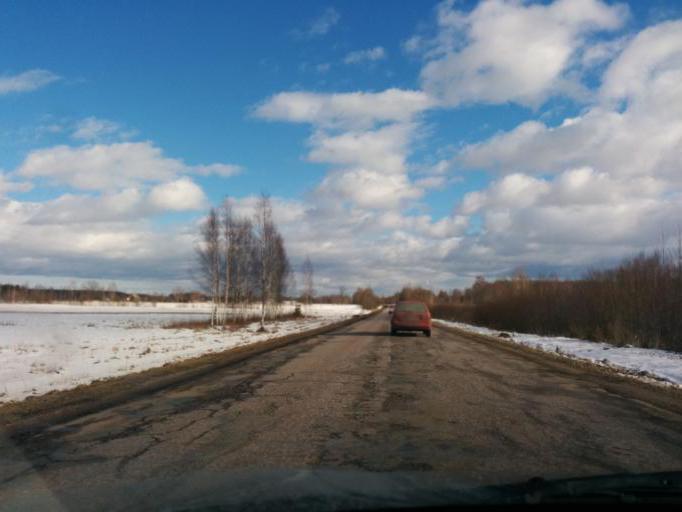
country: LV
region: Balvu Rajons
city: Balvi
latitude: 57.1623
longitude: 27.1748
